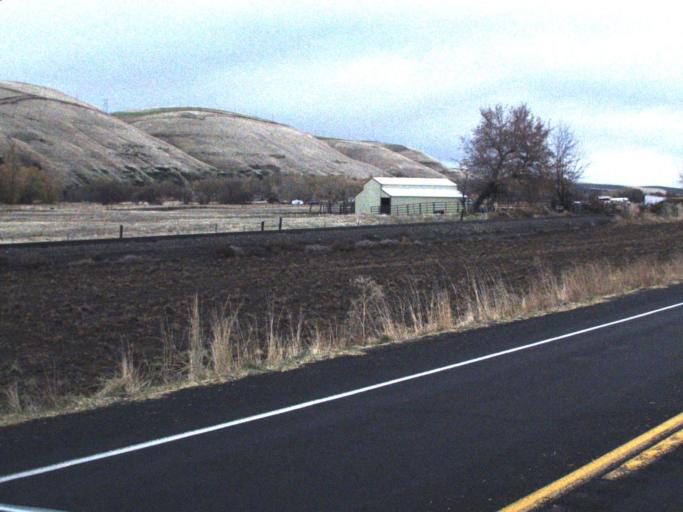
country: US
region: Washington
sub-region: Columbia County
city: Dayton
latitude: 46.2900
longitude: -118.0306
